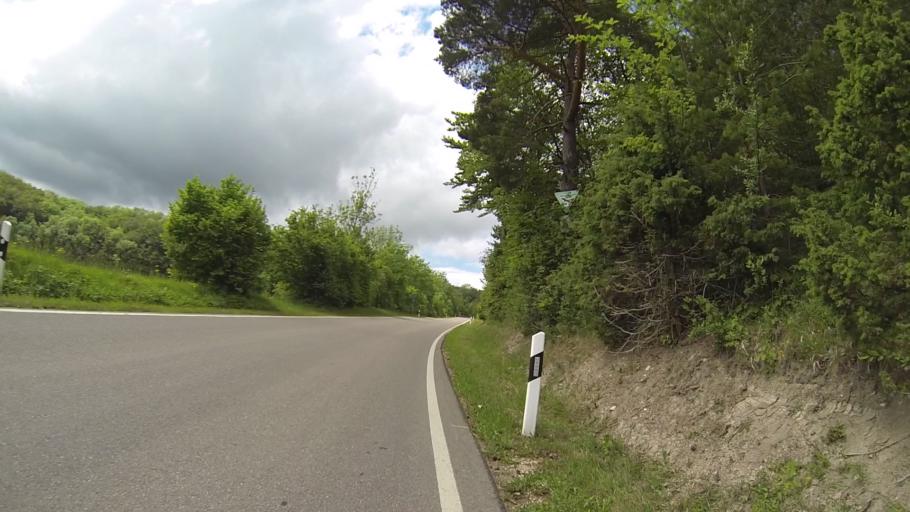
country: DE
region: Baden-Wuerttemberg
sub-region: Regierungsbezirk Stuttgart
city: Waldstetten
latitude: 48.7474
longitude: 9.8695
